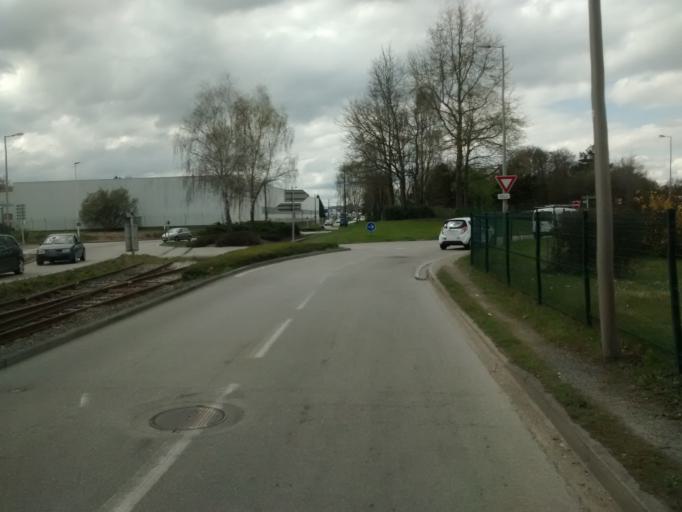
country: FR
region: Brittany
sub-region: Departement du Morbihan
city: Vannes
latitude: 47.6634
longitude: -2.7257
